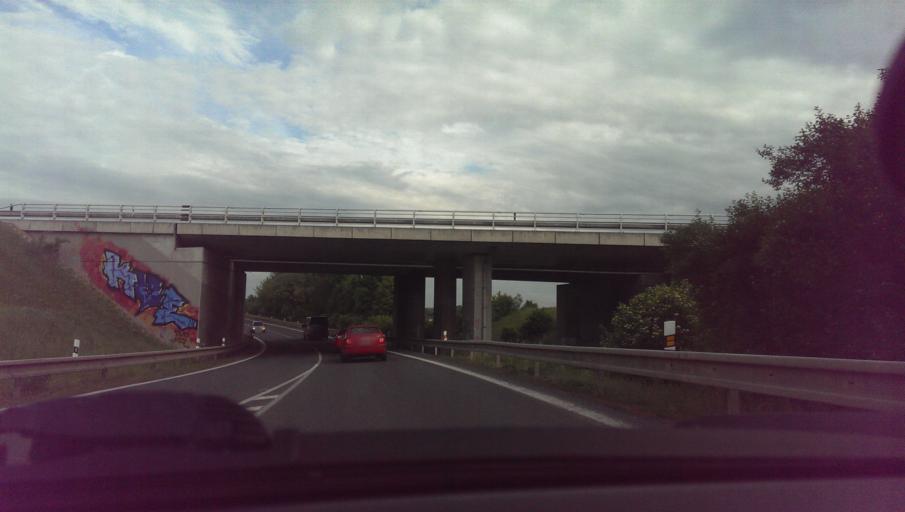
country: CZ
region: Zlin
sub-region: Okres Kromeriz
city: Kromeriz
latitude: 49.3109
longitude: 17.3772
